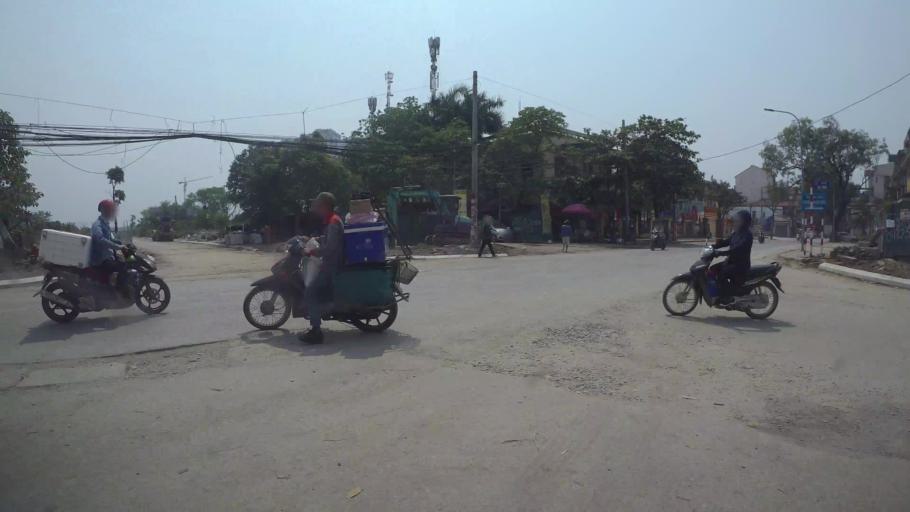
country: VN
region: Ha Noi
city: Ha Dong
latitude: 20.9935
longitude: 105.7610
